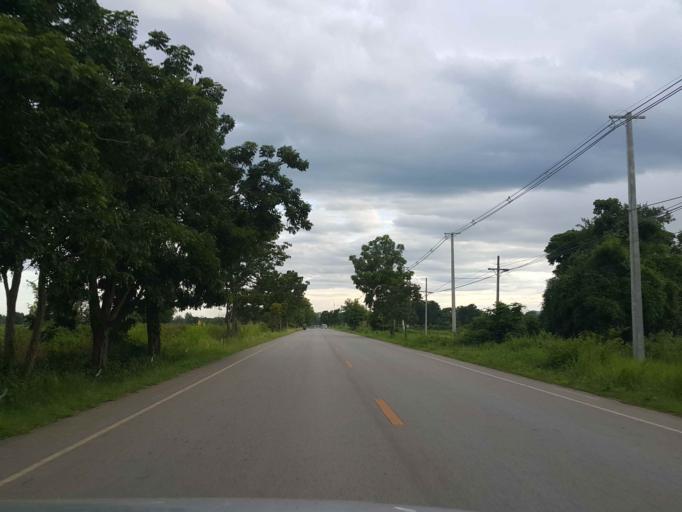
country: TH
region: Sukhothai
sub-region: Amphoe Si Satchanalai
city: Si Satchanalai
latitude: 17.4772
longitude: 99.7404
